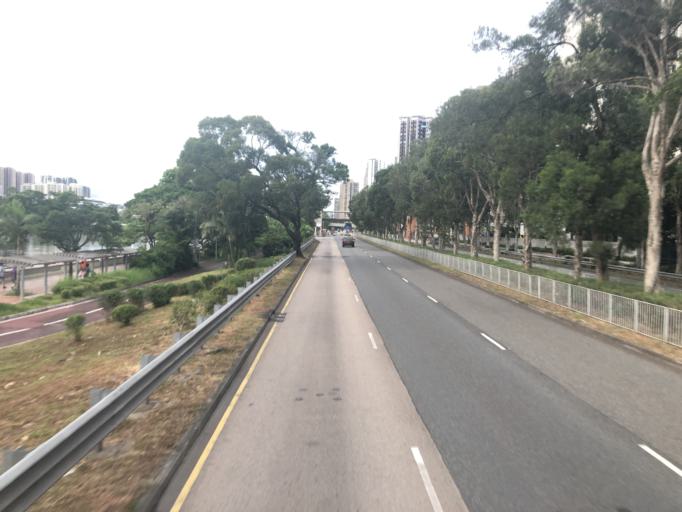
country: HK
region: Sha Tin
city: Sha Tin
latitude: 22.3838
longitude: 114.1969
